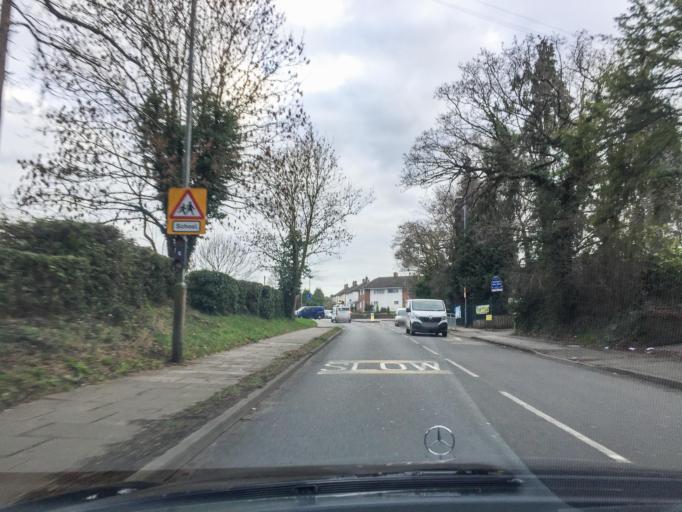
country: GB
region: England
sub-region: City and Borough of Birmingham
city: Bartley Green
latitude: 52.4011
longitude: -1.9616
